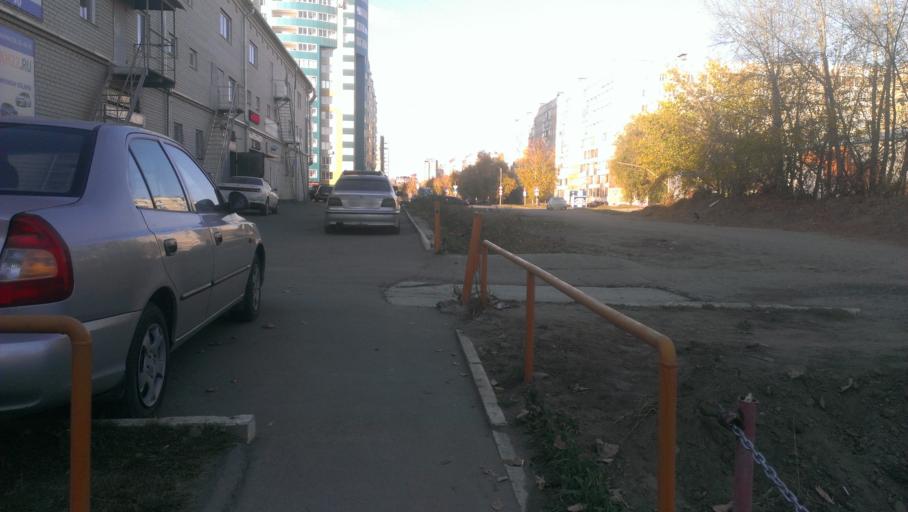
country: RU
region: Altai Krai
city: Novosilikatnyy
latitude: 53.3395
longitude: 83.6610
